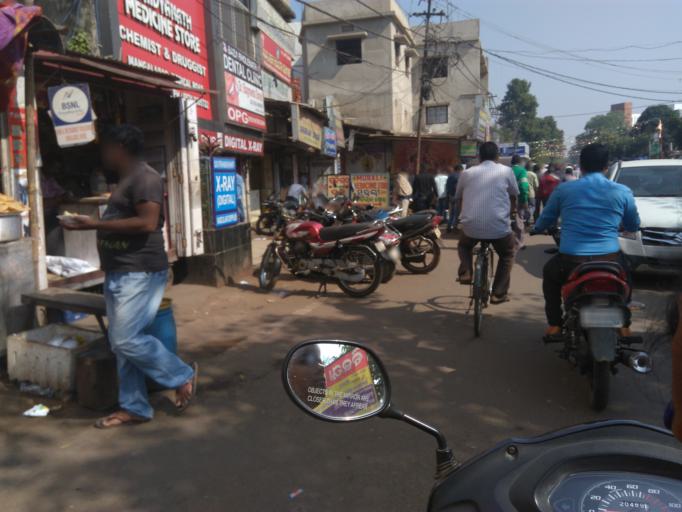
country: IN
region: Odisha
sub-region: Cuttack
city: Cuttack
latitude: 20.4741
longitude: 85.8879
